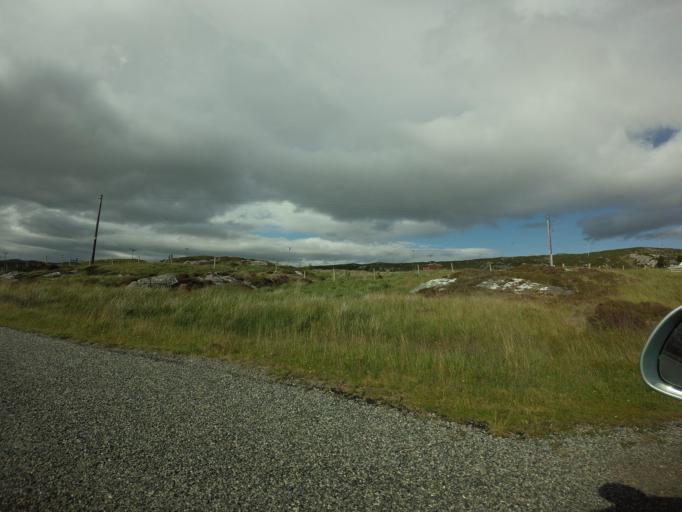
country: GB
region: Scotland
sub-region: Eilean Siar
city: Harris
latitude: 58.1976
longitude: -6.7252
